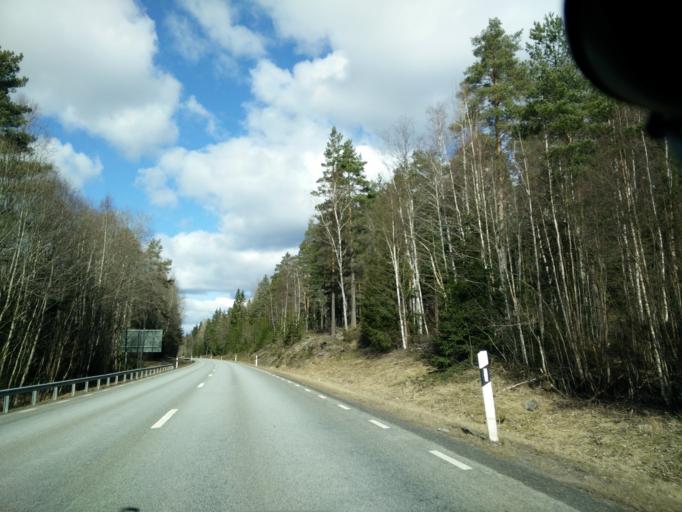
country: SE
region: Vaermland
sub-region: Munkfors Kommun
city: Munkfors
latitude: 59.8509
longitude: 13.5614
